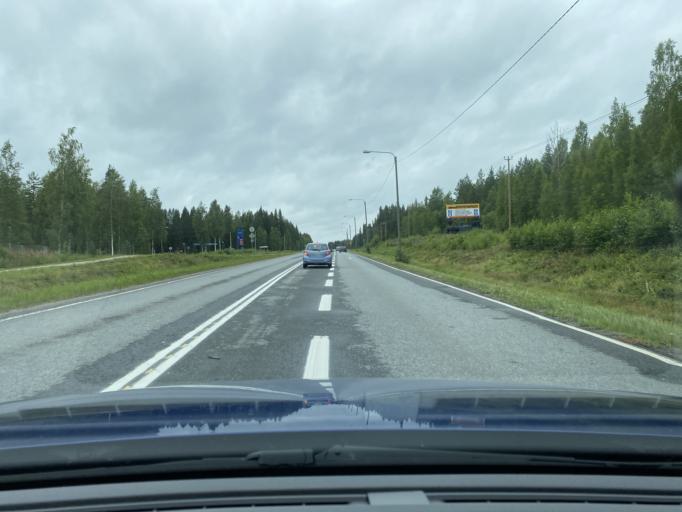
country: FI
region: Central Finland
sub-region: Keuruu
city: Keuruu
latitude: 62.2439
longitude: 24.4781
